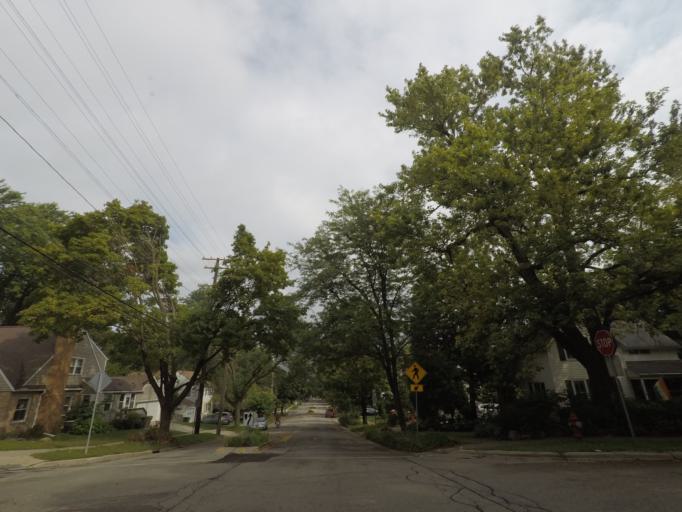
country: US
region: Wisconsin
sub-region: Dane County
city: Shorewood Hills
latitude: 43.0679
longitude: -89.4363
